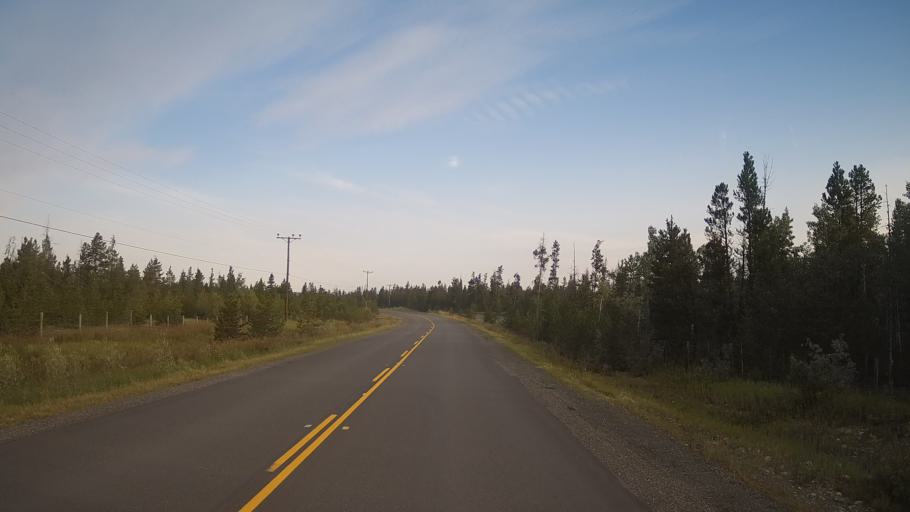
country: CA
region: British Columbia
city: Hanceville
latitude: 52.1354
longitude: -123.7015
